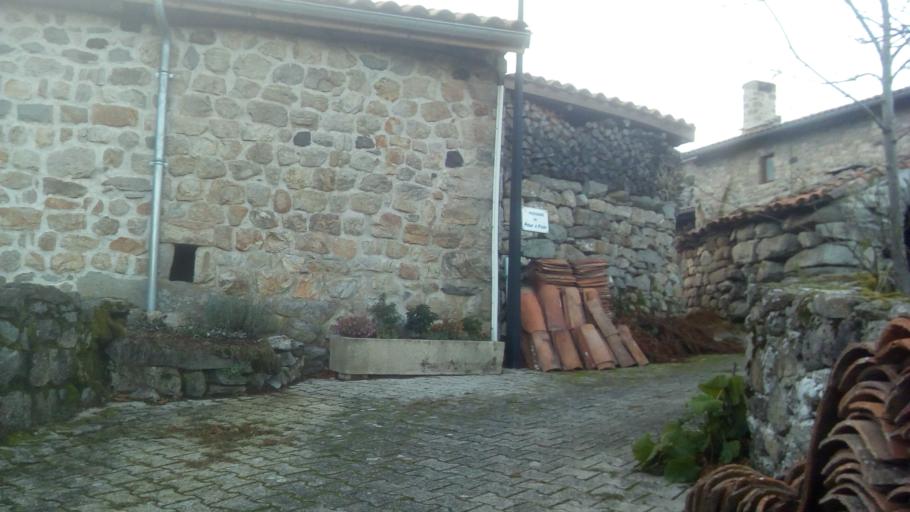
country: FR
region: Rhone-Alpes
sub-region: Departement de l'Ardeche
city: Le Chambon
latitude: 44.8781
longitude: 4.3320
